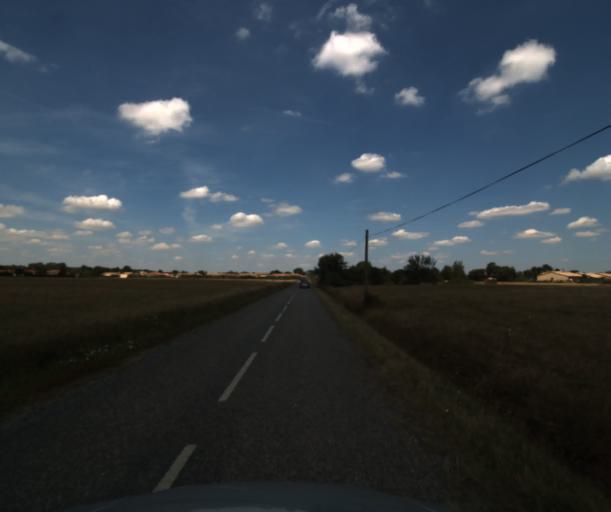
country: FR
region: Midi-Pyrenees
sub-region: Departement de la Haute-Garonne
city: Saint-Lys
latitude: 43.5005
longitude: 1.1762
